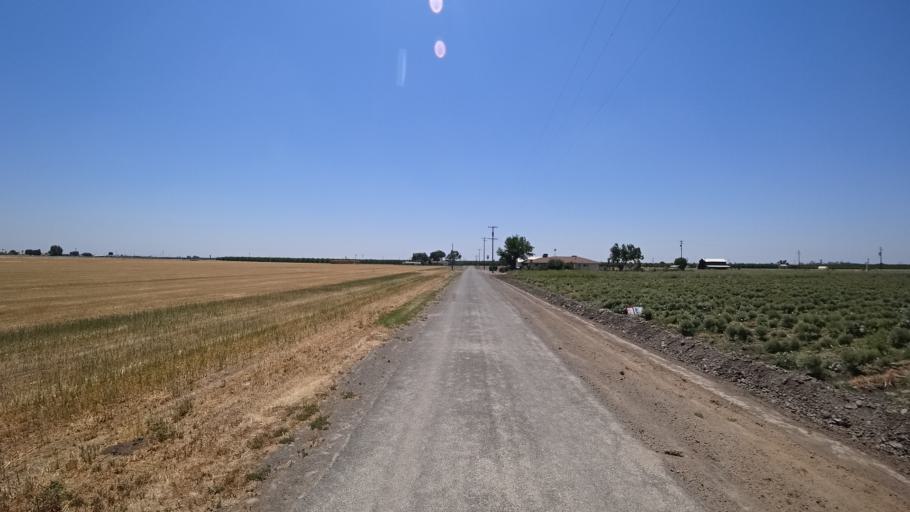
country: US
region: California
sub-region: Fresno County
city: Laton
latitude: 36.3897
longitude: -119.7368
